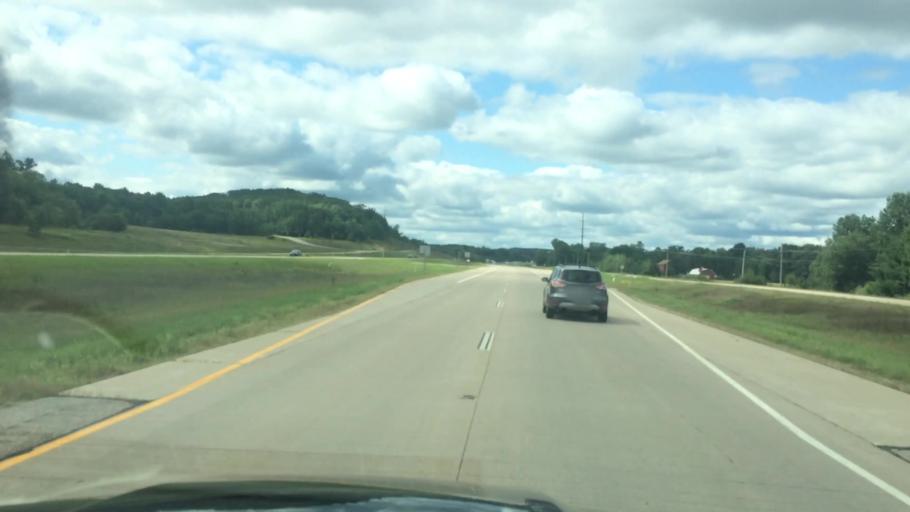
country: US
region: Wisconsin
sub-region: Waupaca County
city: King
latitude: 44.3723
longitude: -89.1515
